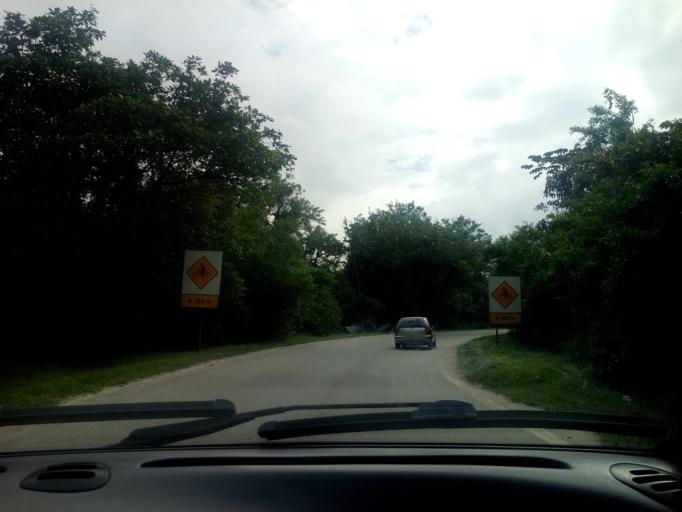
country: BR
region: Sao Paulo
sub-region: Guaruja
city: Guaruja
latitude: -23.9686
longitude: -46.2722
